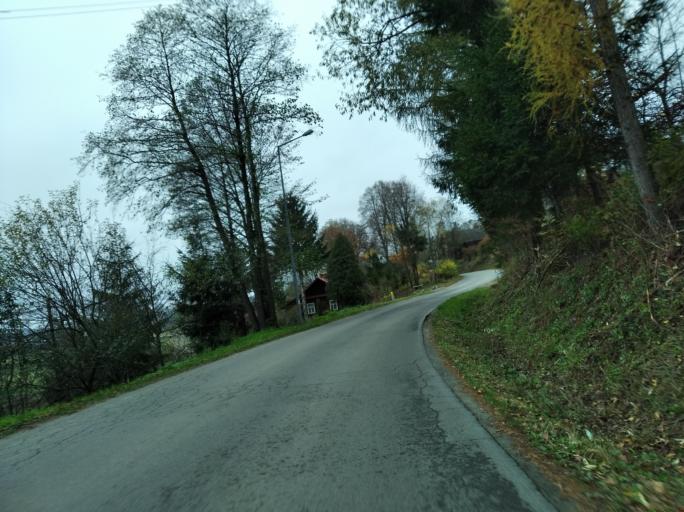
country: PL
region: Subcarpathian Voivodeship
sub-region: Powiat strzyzowski
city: Frysztak
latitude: 49.8288
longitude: 21.6348
